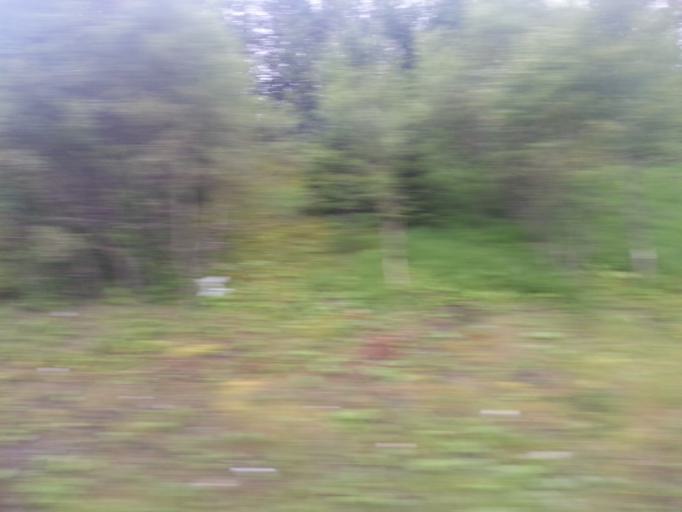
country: NO
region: Sor-Trondelag
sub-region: Malvik
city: Malvik
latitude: 63.4205
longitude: 10.7350
